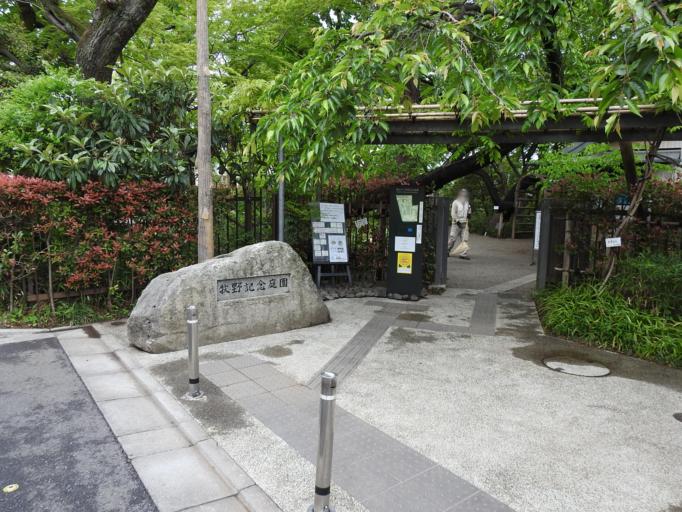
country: JP
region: Tokyo
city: Musashino
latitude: 35.7462
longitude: 139.5858
